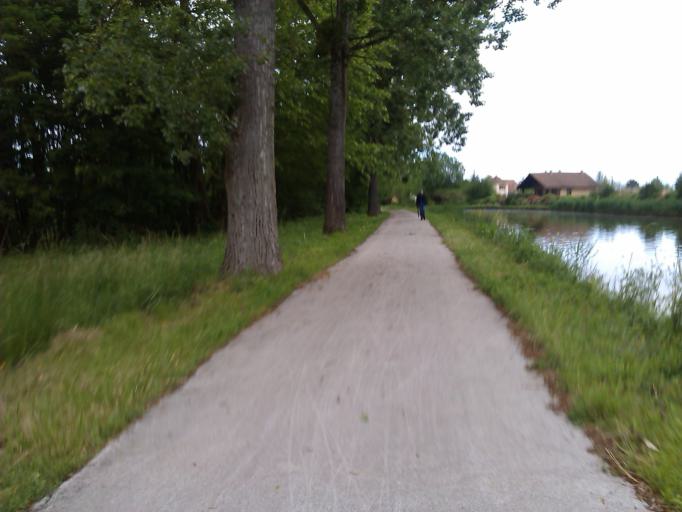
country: FR
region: Bourgogne
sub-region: Departement de Saone-et-Loire
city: Virey-le-Grand
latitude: 46.8281
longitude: 4.8503
